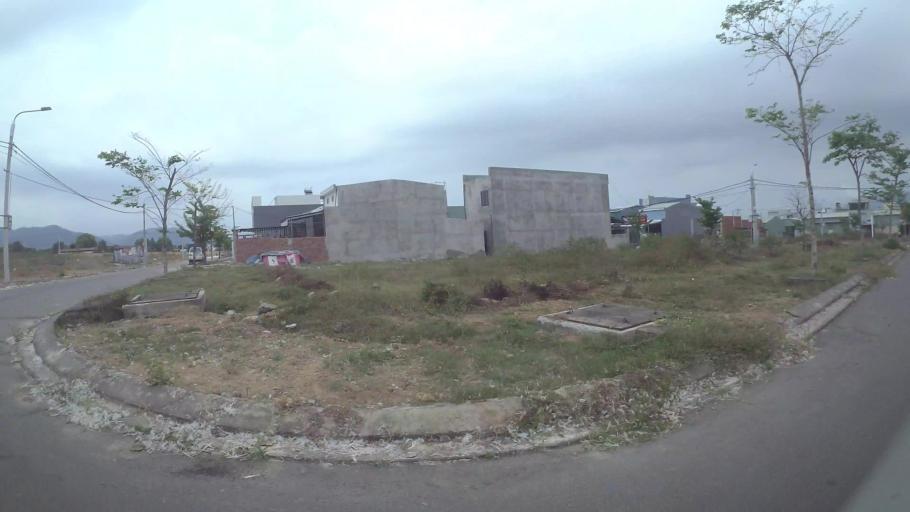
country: VN
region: Da Nang
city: Lien Chieu
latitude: 16.0414
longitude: 108.1677
